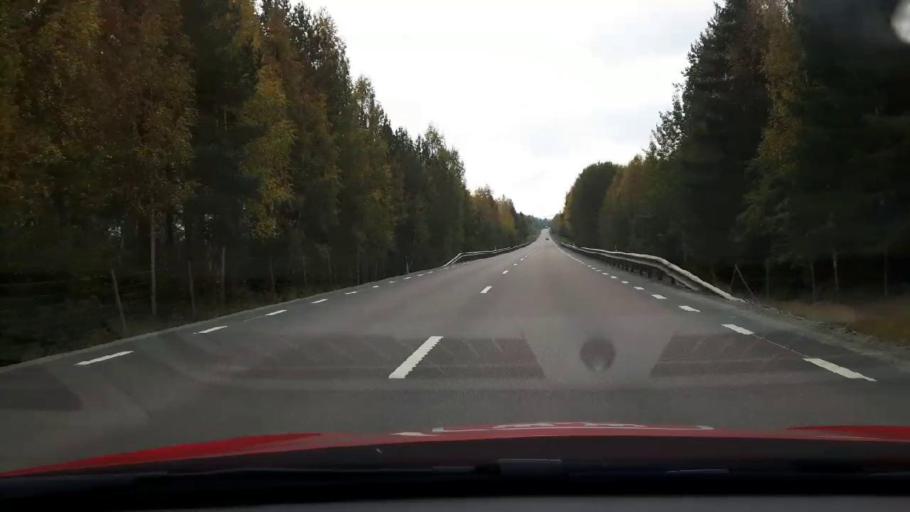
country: SE
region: Gaevleborg
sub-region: Bollnas Kommun
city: Kilafors
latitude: 61.2962
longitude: 16.4904
